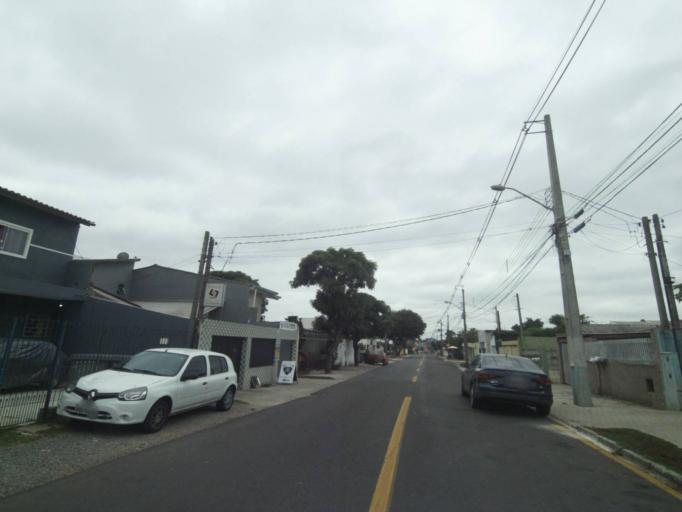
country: BR
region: Parana
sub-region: Sao Jose Dos Pinhais
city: Sao Jose dos Pinhais
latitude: -25.5351
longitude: -49.2633
